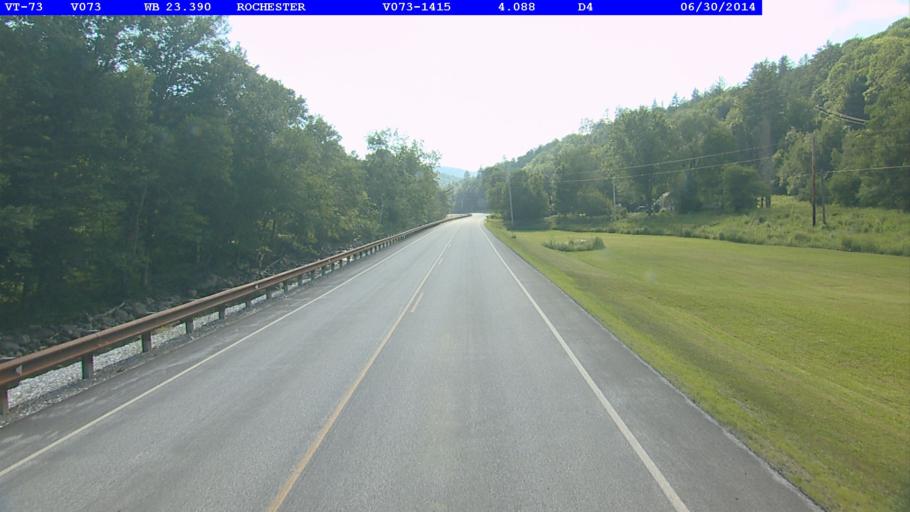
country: US
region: Vermont
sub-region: Rutland County
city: Brandon
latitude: 43.8539
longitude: -72.8896
